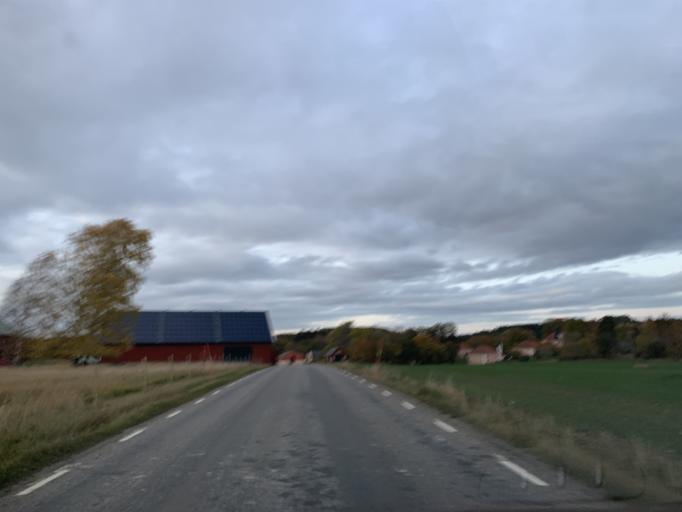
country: SE
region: Stockholm
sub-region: Nynashamns Kommun
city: Osmo
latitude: 58.9554
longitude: 17.7668
